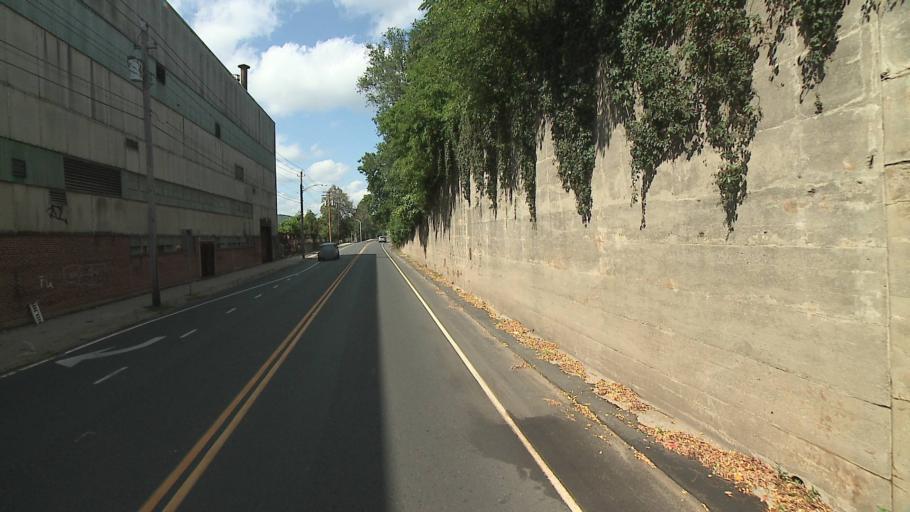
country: US
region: Connecticut
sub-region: New Haven County
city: Ansonia
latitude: 41.3476
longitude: -73.0797
